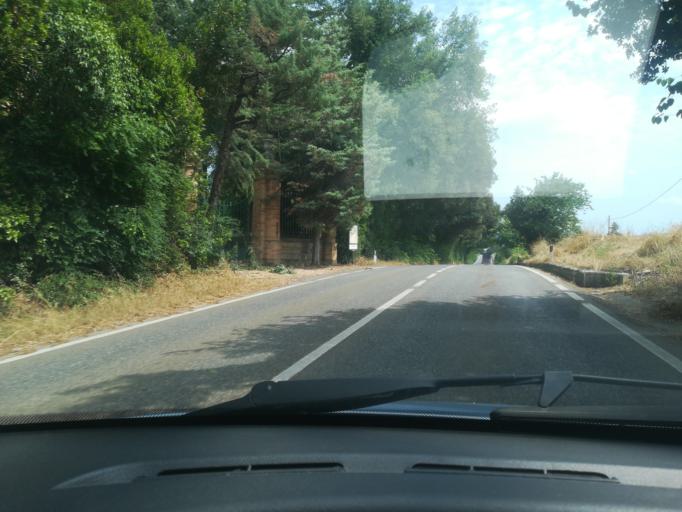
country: IT
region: The Marches
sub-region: Provincia di Macerata
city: Recanati
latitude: 43.3688
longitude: 13.5157
